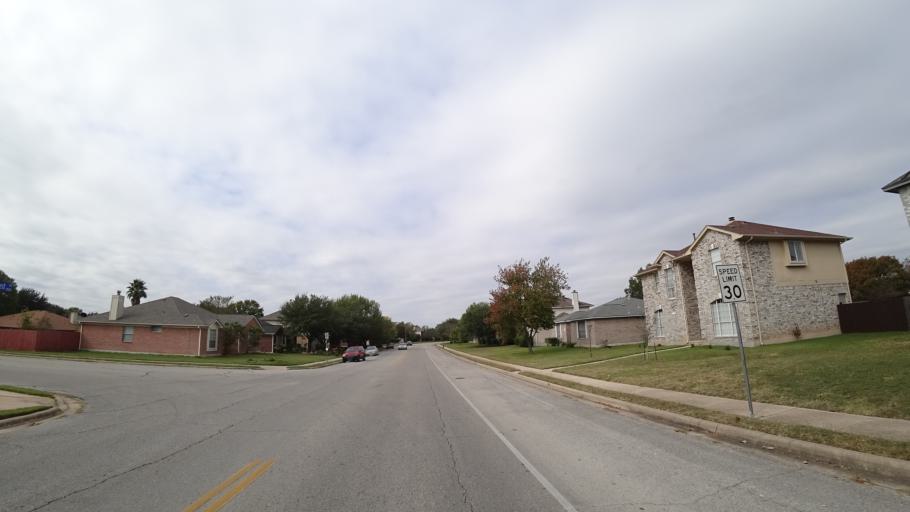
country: US
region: Texas
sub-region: Travis County
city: Windemere
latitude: 30.4621
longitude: -97.6420
